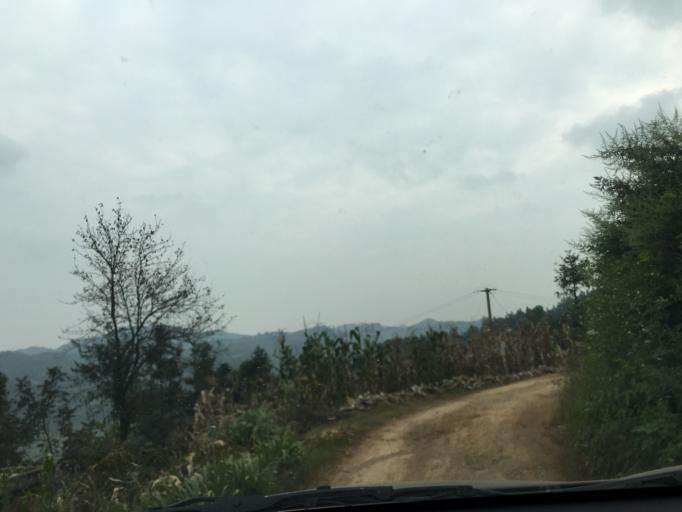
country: CN
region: Guangxi Zhuangzu Zizhiqu
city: Xinzhou
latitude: 25.5387
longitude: 105.5284
